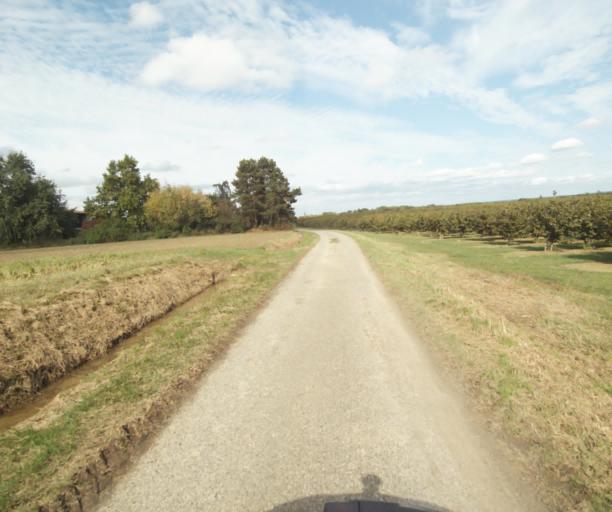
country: FR
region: Midi-Pyrenees
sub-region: Departement du Tarn-et-Garonne
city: Verdun-sur-Garonne
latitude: 43.8746
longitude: 1.1954
